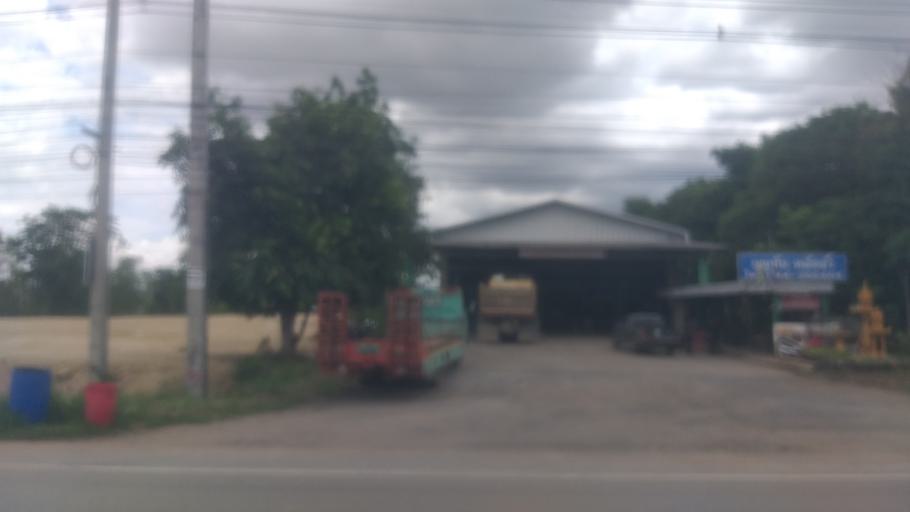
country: TH
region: Nakhon Ratchasima
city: Nakhon Ratchasima
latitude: 15.0609
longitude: 102.1242
